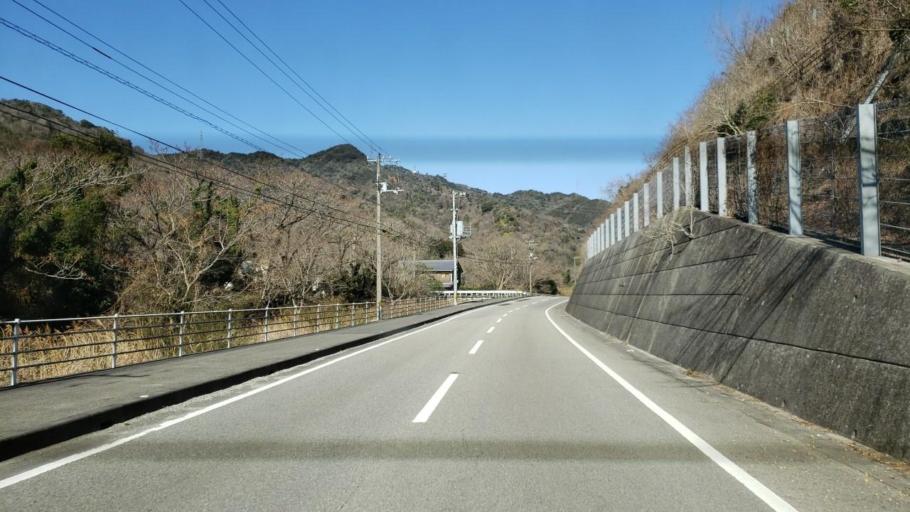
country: JP
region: Tokushima
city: Narutocho-mitsuishi
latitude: 34.1697
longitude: 134.5410
